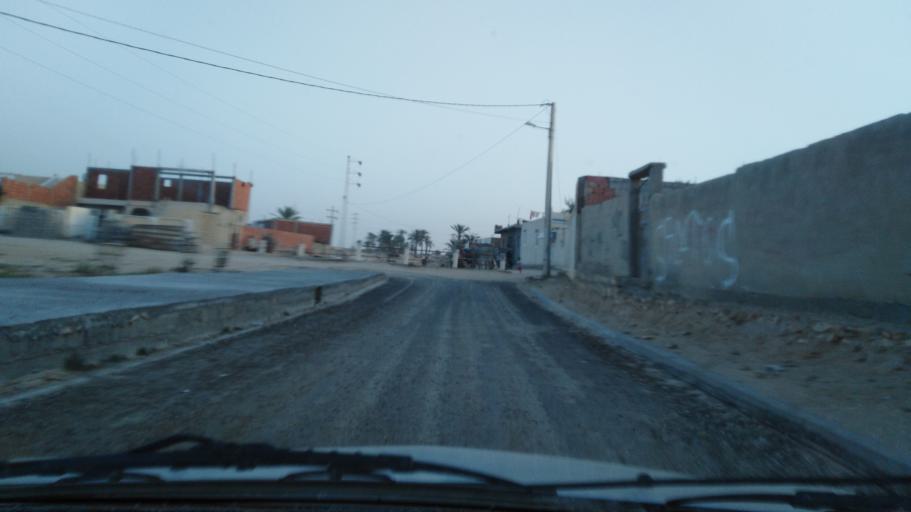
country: TN
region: Qabis
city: Gabes
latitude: 33.9551
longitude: 9.9949
